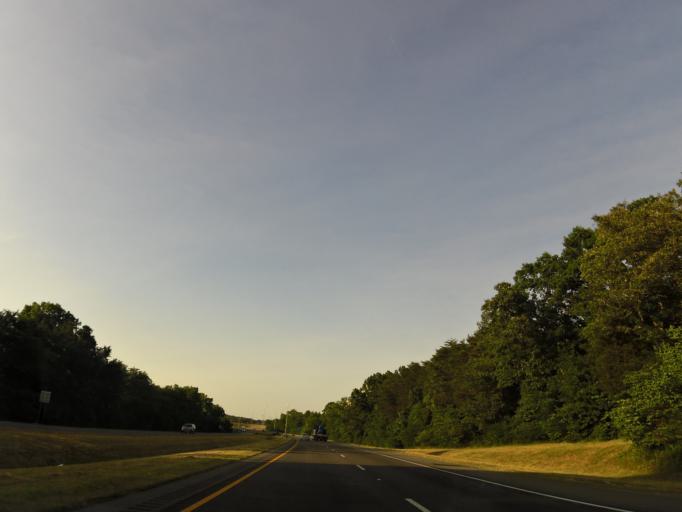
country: US
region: Alabama
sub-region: DeKalb County
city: Fort Payne
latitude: 34.4957
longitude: -85.6960
